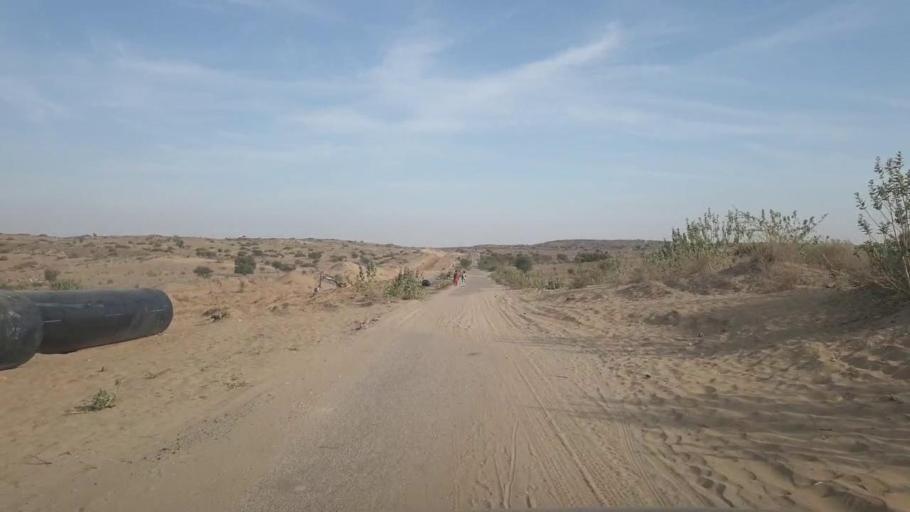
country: PK
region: Sindh
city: Nabisar
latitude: 25.0627
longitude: 69.6561
